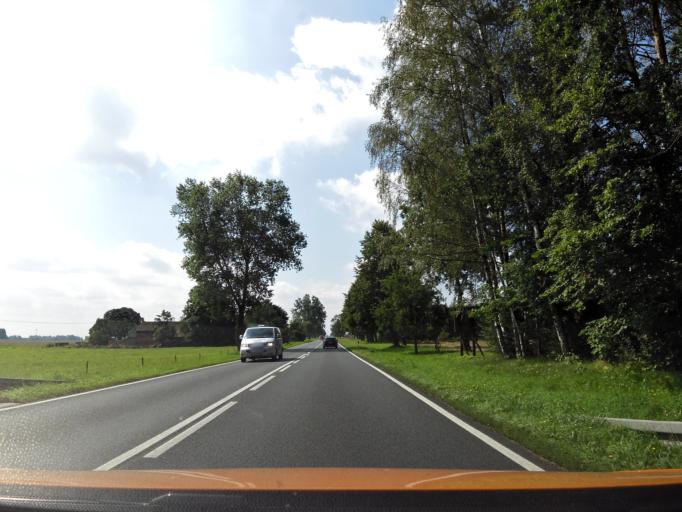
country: PL
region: West Pomeranian Voivodeship
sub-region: Powiat gryficki
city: Ploty
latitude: 53.7375
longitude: 15.2080
